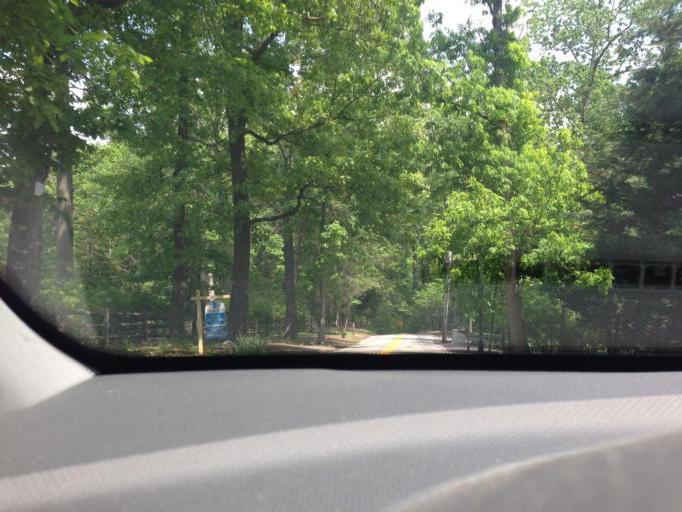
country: US
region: Maryland
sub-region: Baltimore County
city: Cockeysville
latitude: 39.4764
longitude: -76.6874
